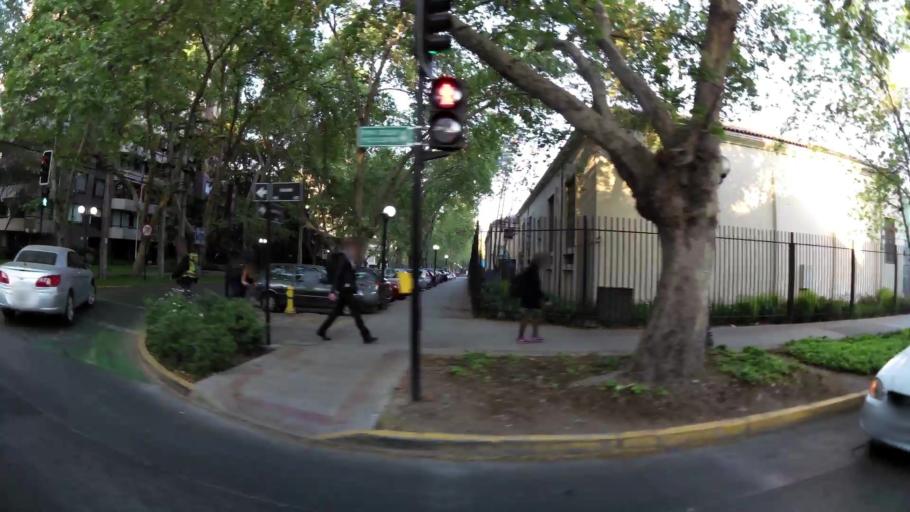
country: CL
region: Santiago Metropolitan
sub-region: Provincia de Santiago
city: Villa Presidente Frei, Nunoa, Santiago, Chile
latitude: -33.4246
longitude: -70.6022
